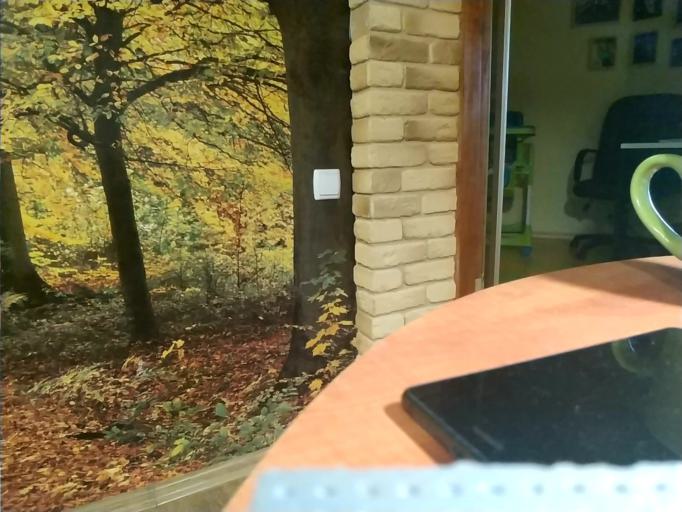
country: RU
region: Moskovskaya
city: Klin
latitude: 56.3509
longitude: 36.7483
